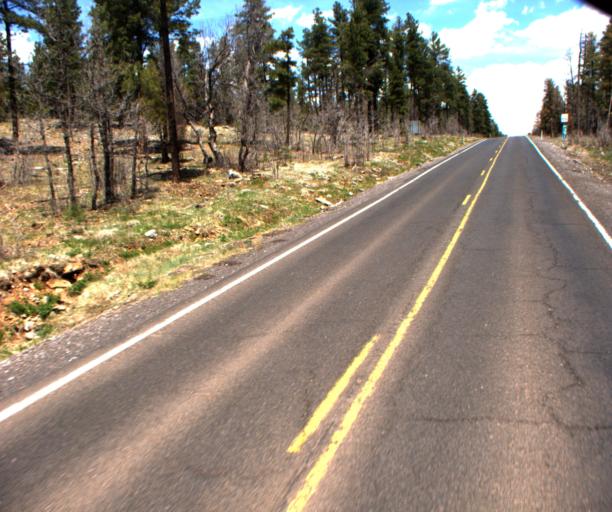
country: US
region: Arizona
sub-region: Coconino County
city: Kachina Village
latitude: 35.0448
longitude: -111.7334
